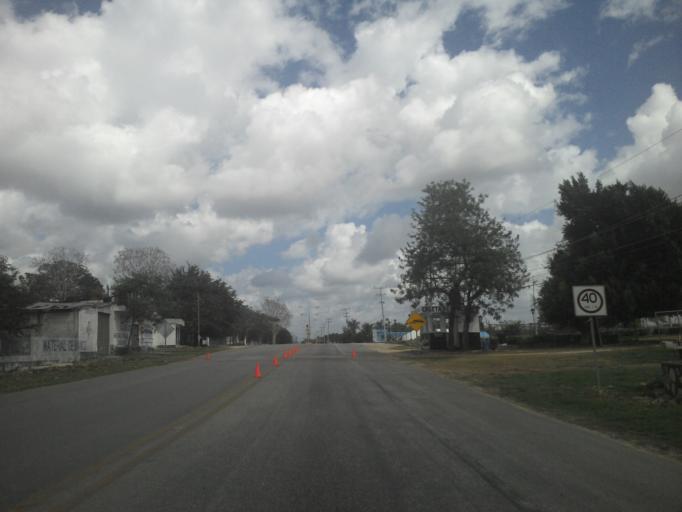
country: MX
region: Yucatan
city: Temozon
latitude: 20.7936
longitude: -88.2020
